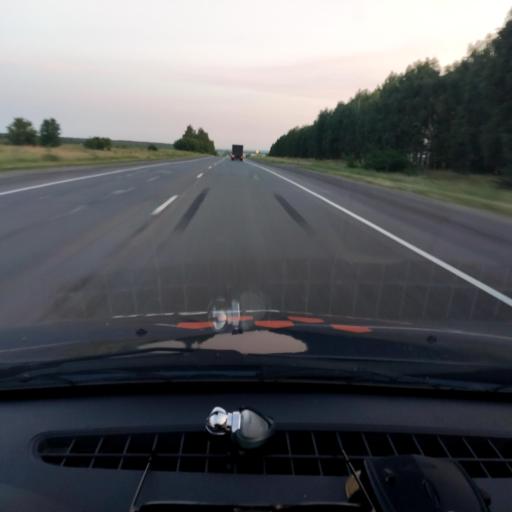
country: RU
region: Kursk
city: Gorshechnoye
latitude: 51.4549
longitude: 37.9192
